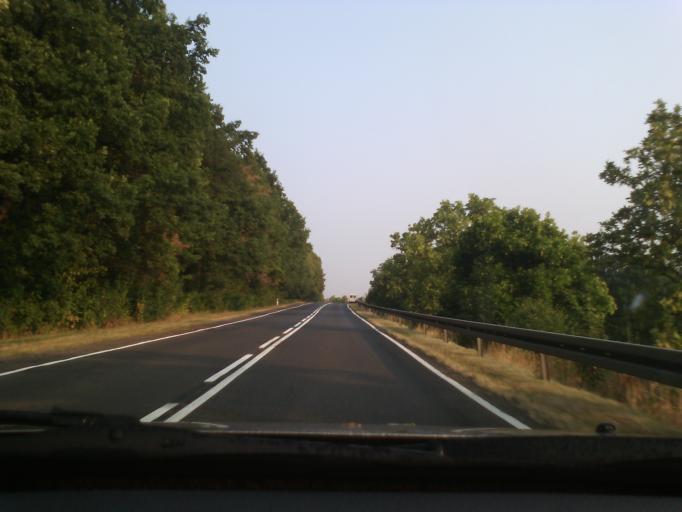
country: PL
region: Lower Silesian Voivodeship
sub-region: Powiat walbrzyski
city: Stare Bogaczowice
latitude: 50.9034
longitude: 16.2534
